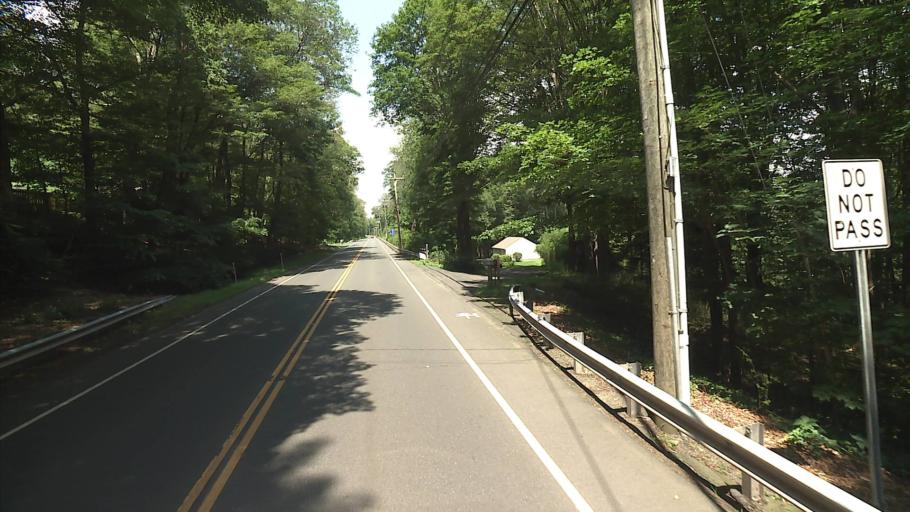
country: US
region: Connecticut
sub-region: Middlesex County
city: East Haddam
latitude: 41.4323
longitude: -72.4549
